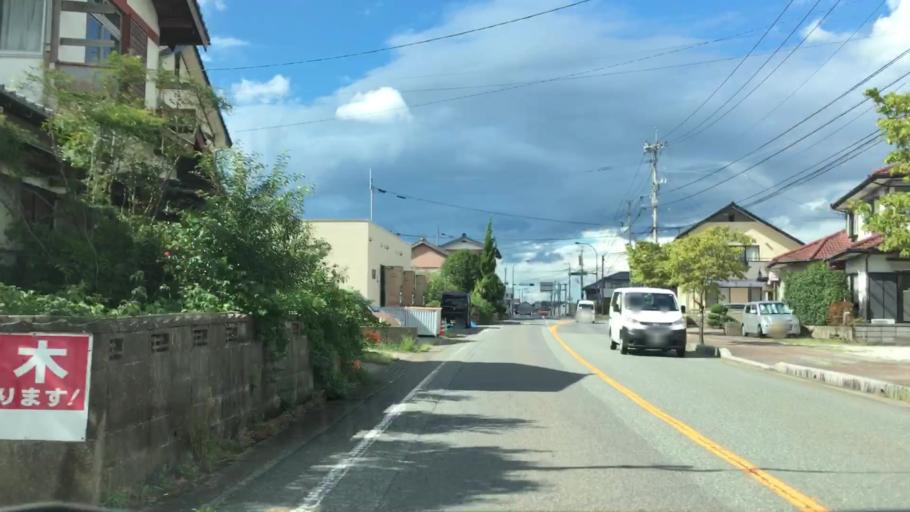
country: JP
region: Saga Prefecture
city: Imaricho-ko
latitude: 33.1946
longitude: 129.8507
